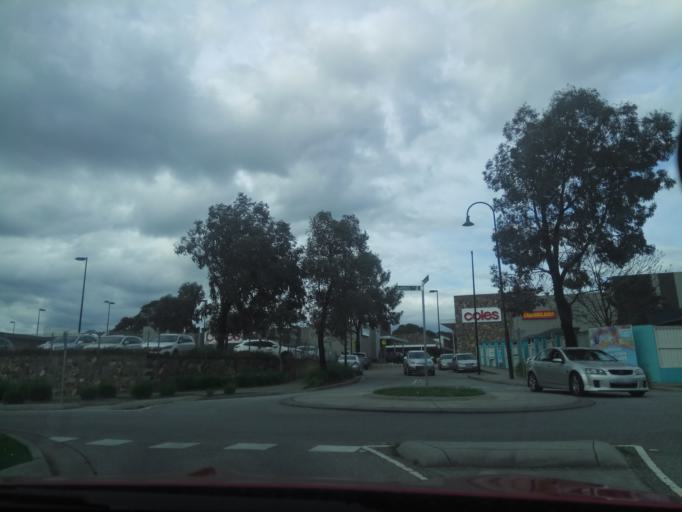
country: AU
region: Victoria
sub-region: Casey
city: Lynbrook
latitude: -38.0524
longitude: 145.2557
